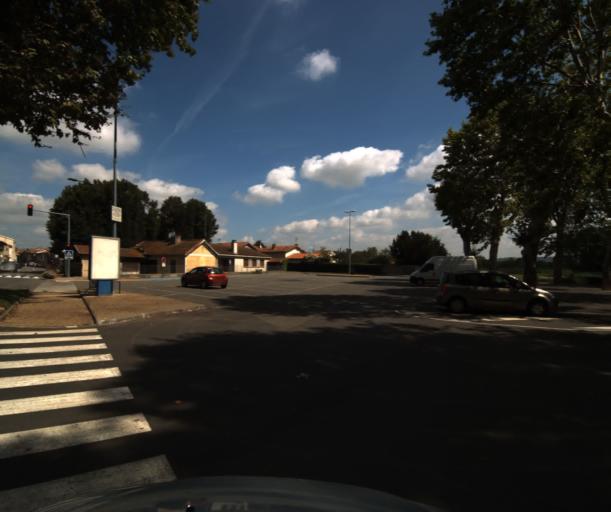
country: FR
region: Midi-Pyrenees
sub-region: Departement de la Haute-Garonne
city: Pinsaguel
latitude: 43.5066
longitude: 1.3907
